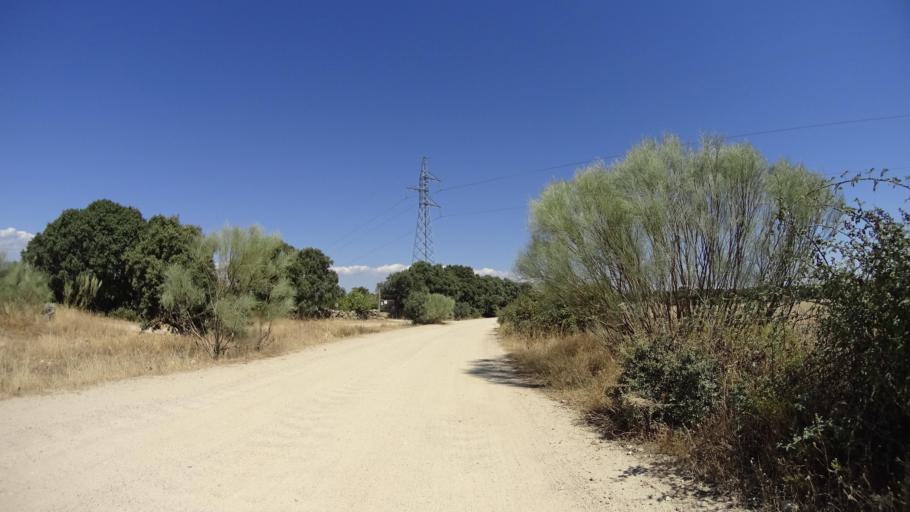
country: ES
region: Madrid
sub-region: Provincia de Madrid
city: Colmenarejo
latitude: 40.5359
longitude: -4.0104
